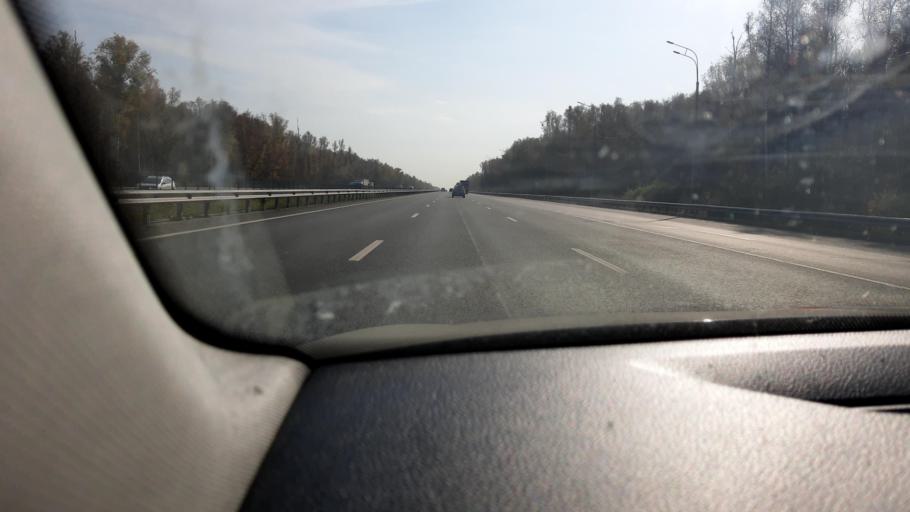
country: RU
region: Moskovskaya
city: Stupino
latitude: 54.9150
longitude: 38.0038
